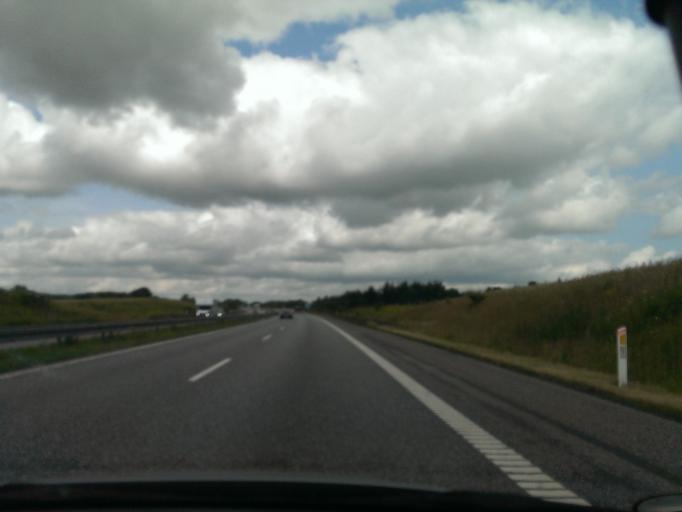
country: DK
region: North Denmark
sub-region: Mariagerfjord Kommune
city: Hobro
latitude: 56.5660
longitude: 9.8594
